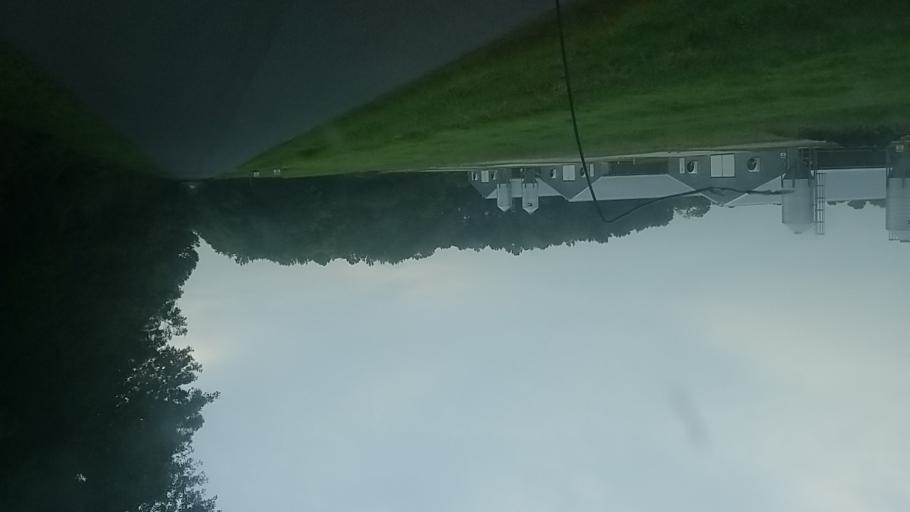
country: US
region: Maryland
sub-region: Wicomico County
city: Pittsville
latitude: 38.4521
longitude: -75.3895
